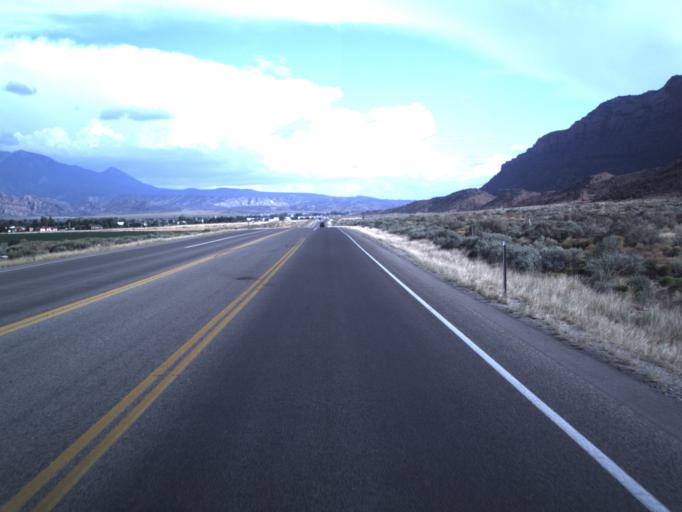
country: US
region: Utah
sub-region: Grand County
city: Moab
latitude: 38.5127
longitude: -109.4881
